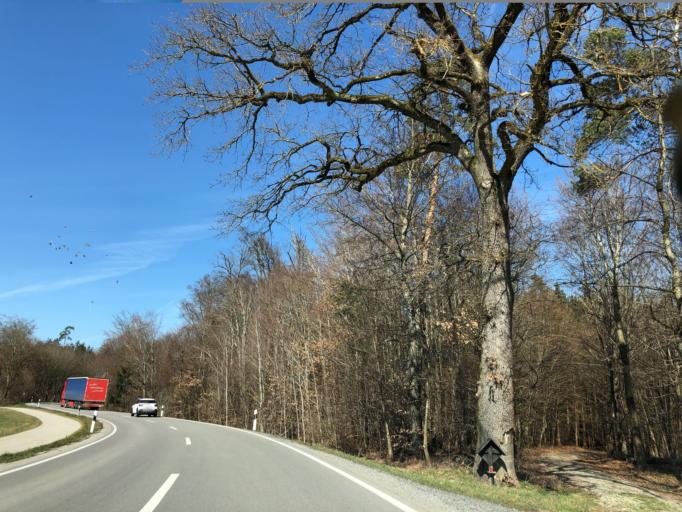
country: DE
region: Bavaria
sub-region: Upper Bavaria
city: Pfaffing
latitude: 48.0726
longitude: 12.1069
